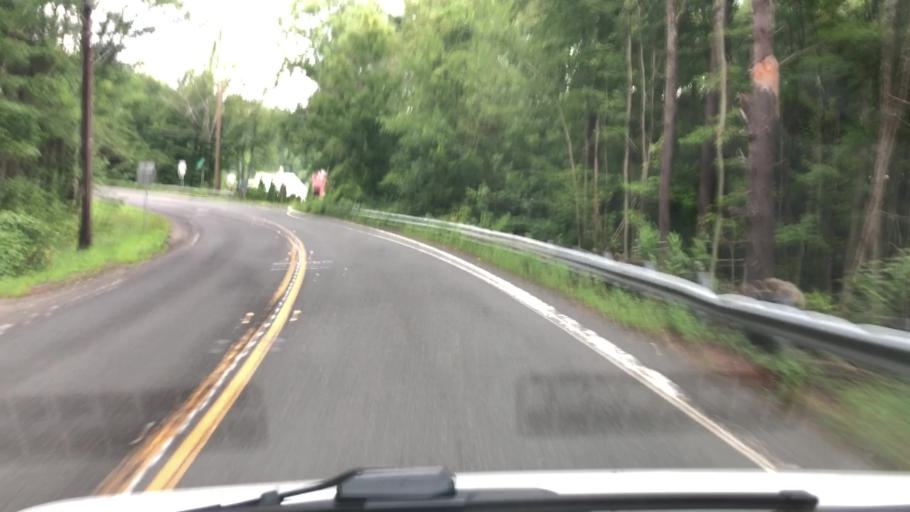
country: US
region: Massachusetts
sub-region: Franklin County
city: Conway
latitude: 42.5125
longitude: -72.6681
